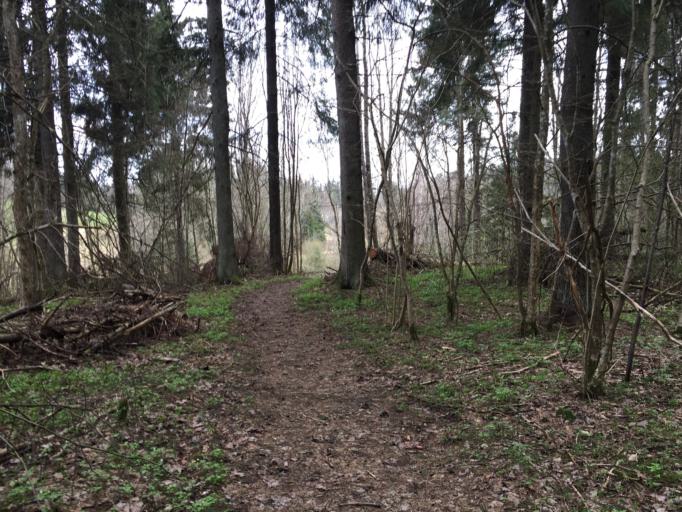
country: EE
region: Vorumaa
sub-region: Voru linn
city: Voru
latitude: 57.7134
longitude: 27.0620
